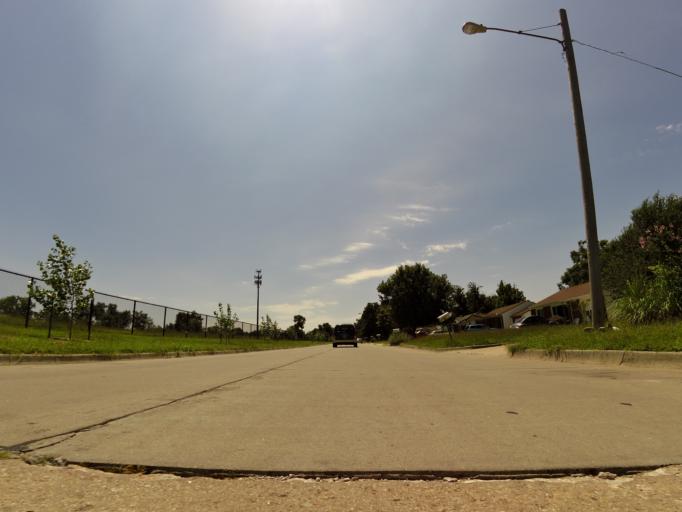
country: US
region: Kansas
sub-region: Sedgwick County
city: Wichita
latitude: 37.7048
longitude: -97.2917
